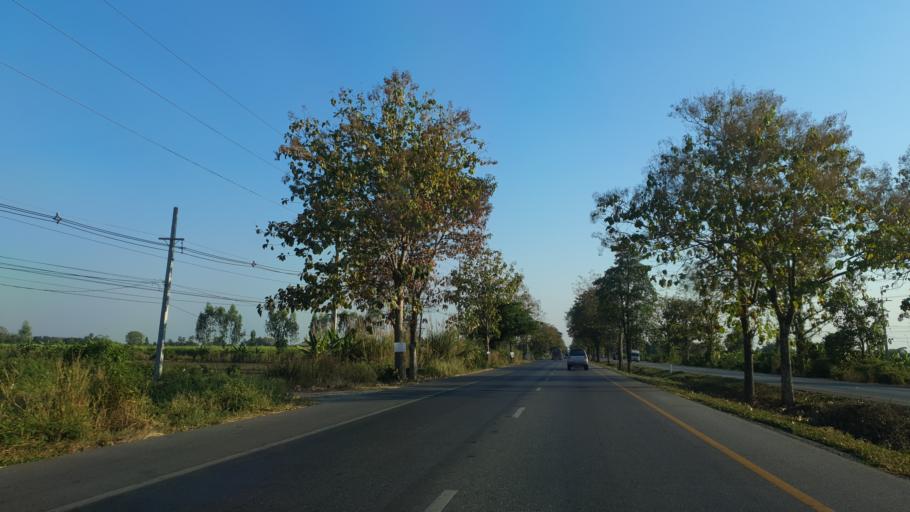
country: TH
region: Kamphaeng Phet
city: Khlong Khlung
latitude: 16.2486
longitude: 99.6909
